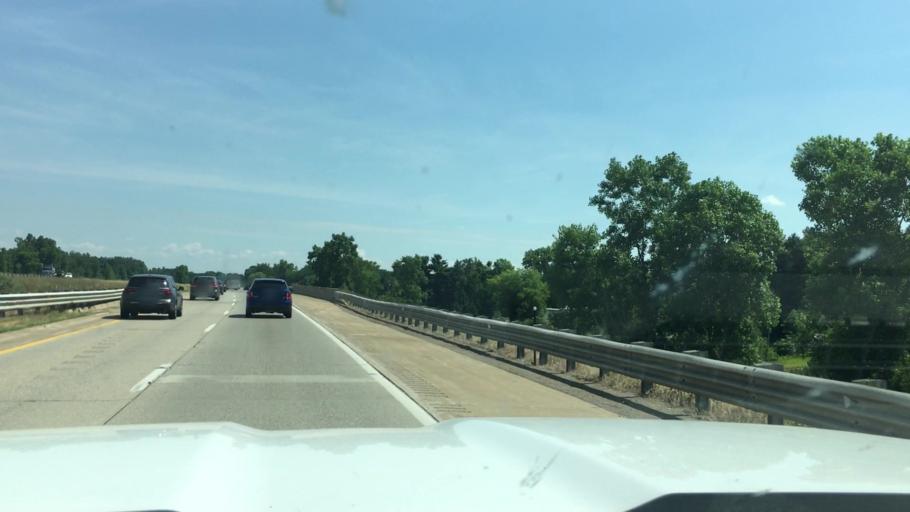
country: US
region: Michigan
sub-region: Shiawassee County
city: Perry
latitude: 42.8191
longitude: -84.2714
